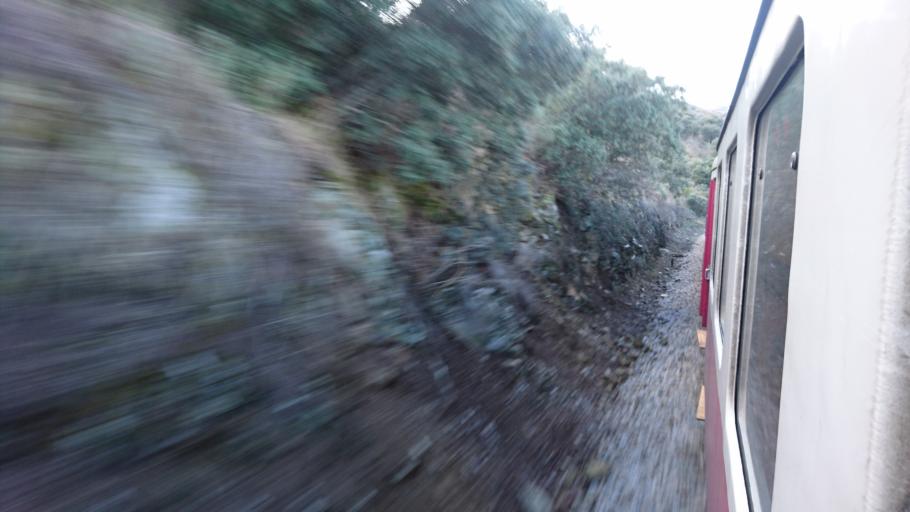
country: PT
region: Guarda
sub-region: Vila Nova de Foz Coa
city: Vila Nova de Foz Coa
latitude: 41.1271
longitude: -7.1575
